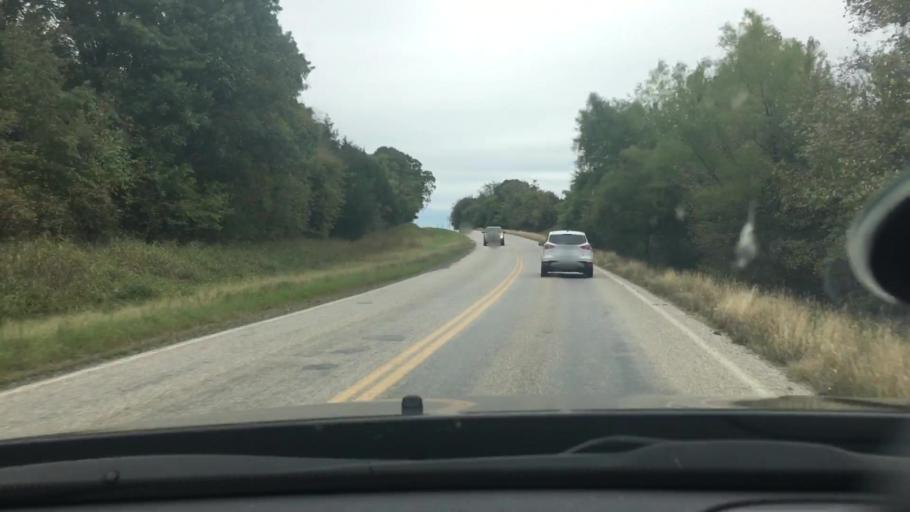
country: US
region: Oklahoma
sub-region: Johnston County
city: Tishomingo
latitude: 34.3334
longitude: -96.4195
